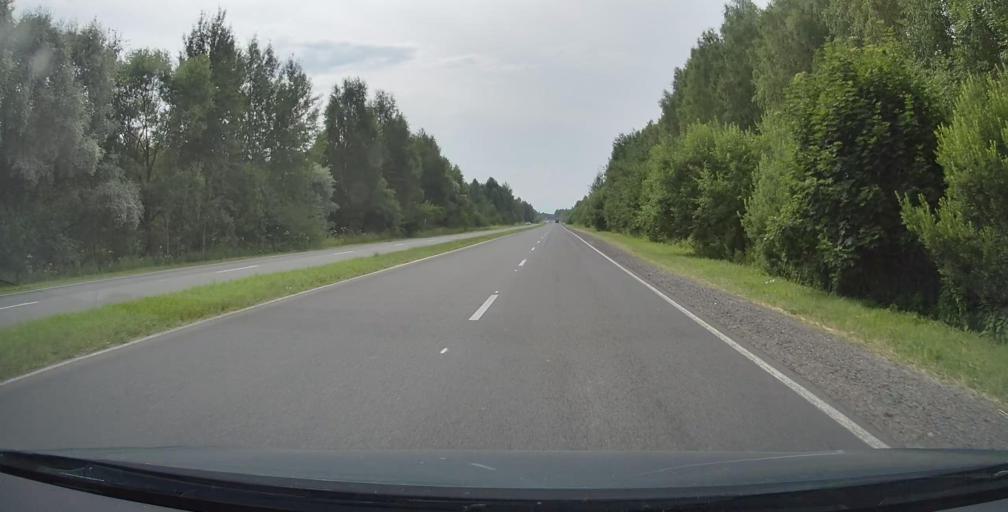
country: RU
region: Jaroslavl
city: Rybinsk
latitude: 58.0100
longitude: 38.9218
